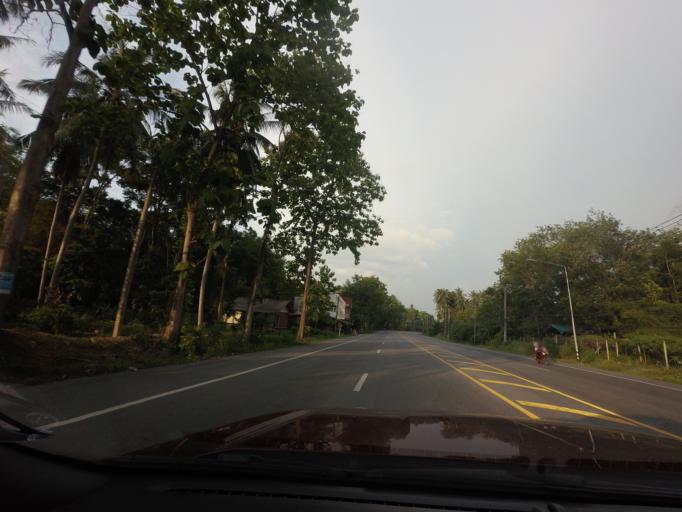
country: TH
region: Pattani
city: Khok Pho
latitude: 6.6768
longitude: 101.1342
